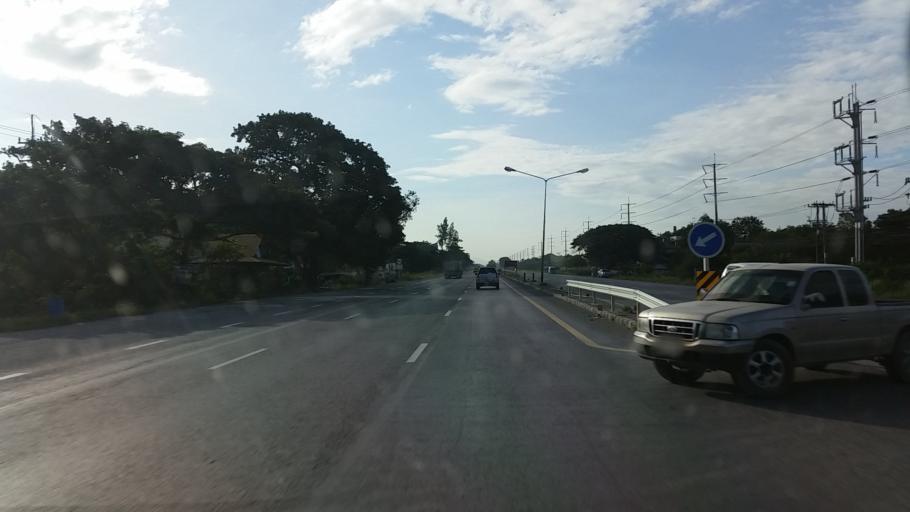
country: TH
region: Sara Buri
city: Chaloem Phra Kiat
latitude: 14.6227
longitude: 100.8909
